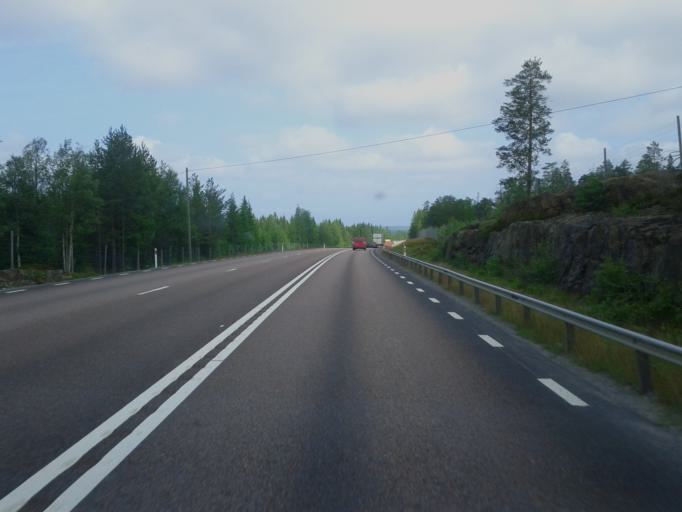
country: SE
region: Vaesterbotten
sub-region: Skelleftea Kommun
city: Burea
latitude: 64.4441
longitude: 21.2831
